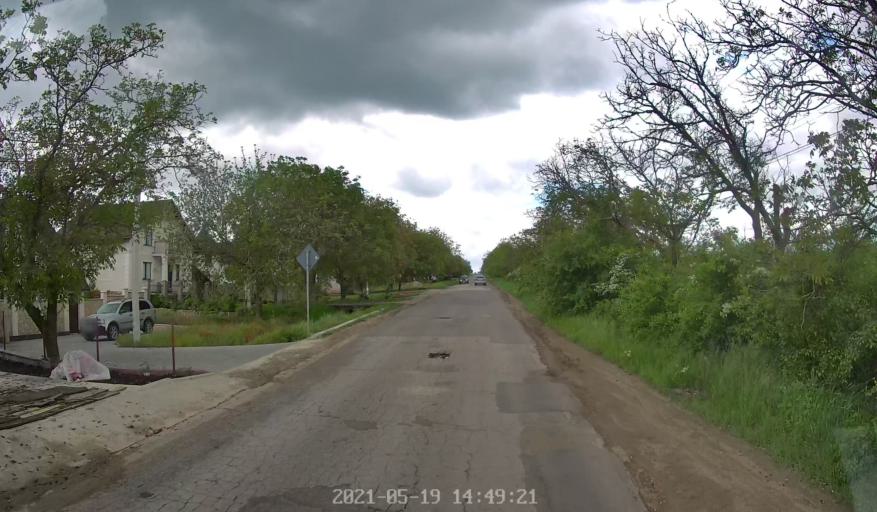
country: MD
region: Chisinau
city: Stauceni
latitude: 47.0493
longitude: 28.9522
